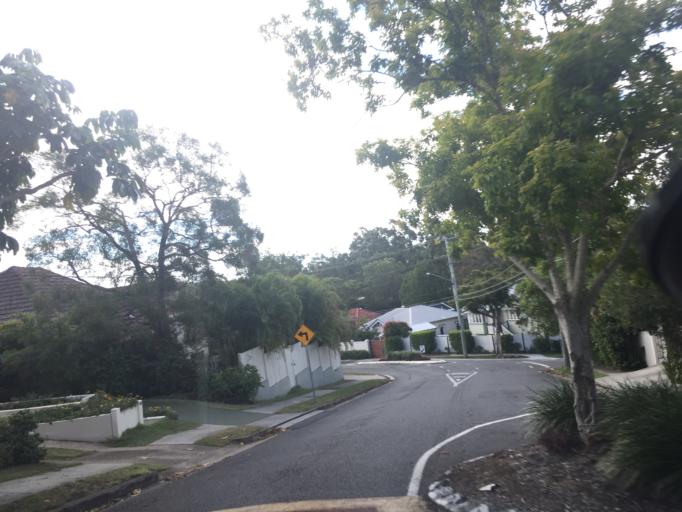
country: AU
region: Queensland
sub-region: Brisbane
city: Milton
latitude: -27.4504
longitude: 152.9753
